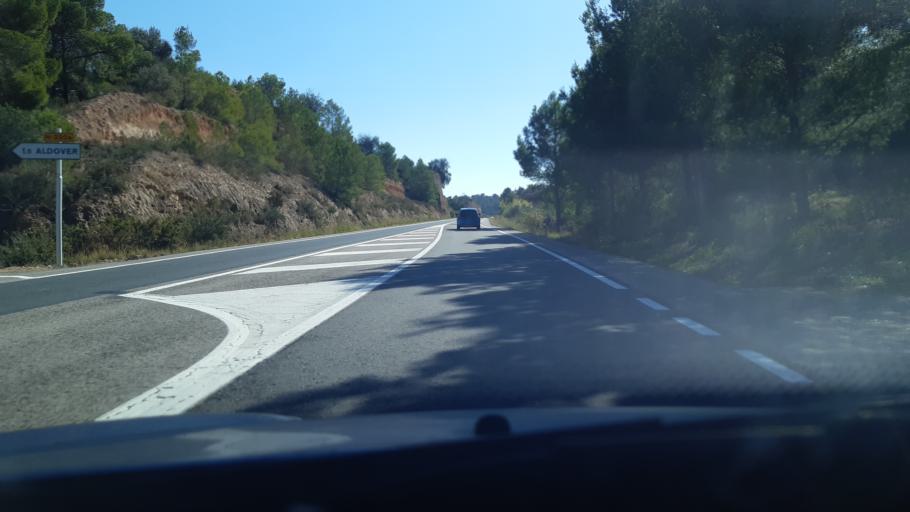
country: ES
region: Catalonia
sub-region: Provincia de Tarragona
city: Tivenys
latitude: 40.8897
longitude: 0.4906
